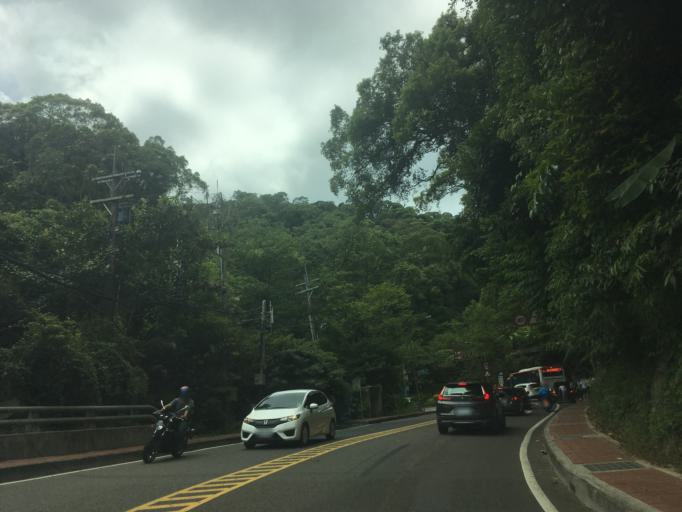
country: TW
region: Taiwan
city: Daxi
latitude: 24.8364
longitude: 121.3025
